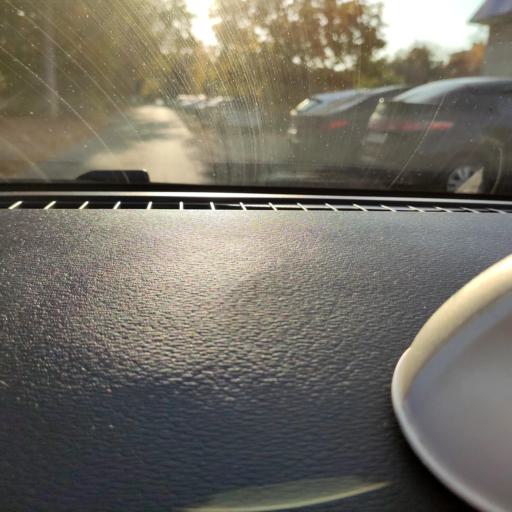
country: RU
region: Samara
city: Samara
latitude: 53.2188
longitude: 50.2333
